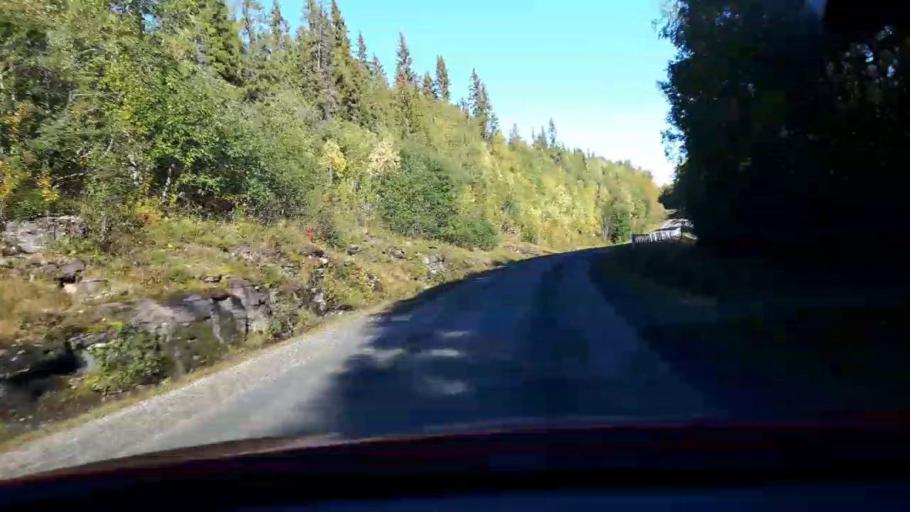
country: NO
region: Nord-Trondelag
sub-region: Lierne
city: Sandvika
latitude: 64.5695
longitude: 13.9040
